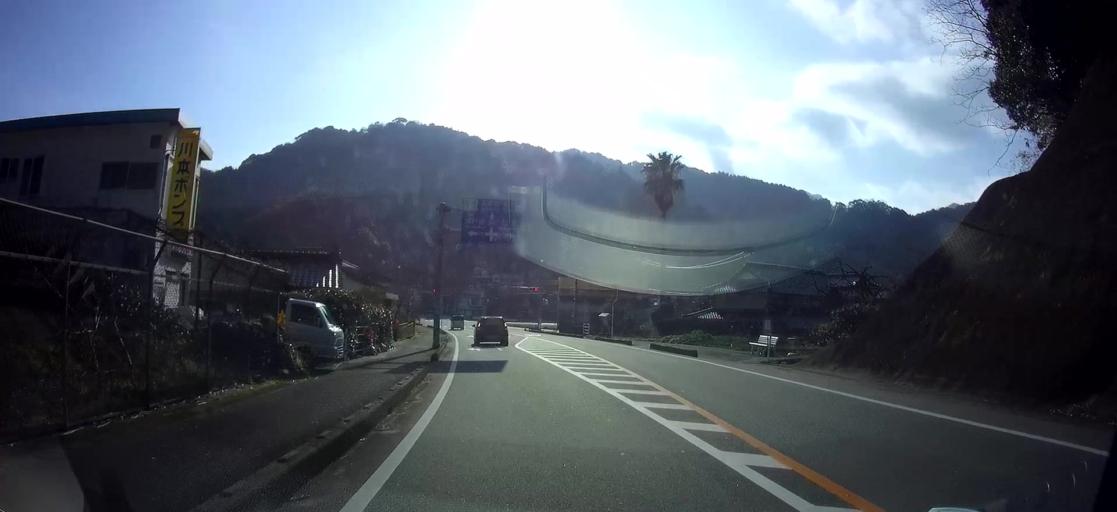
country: JP
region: Kumamoto
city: Yatsushiro
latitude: 32.4420
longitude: 130.4064
